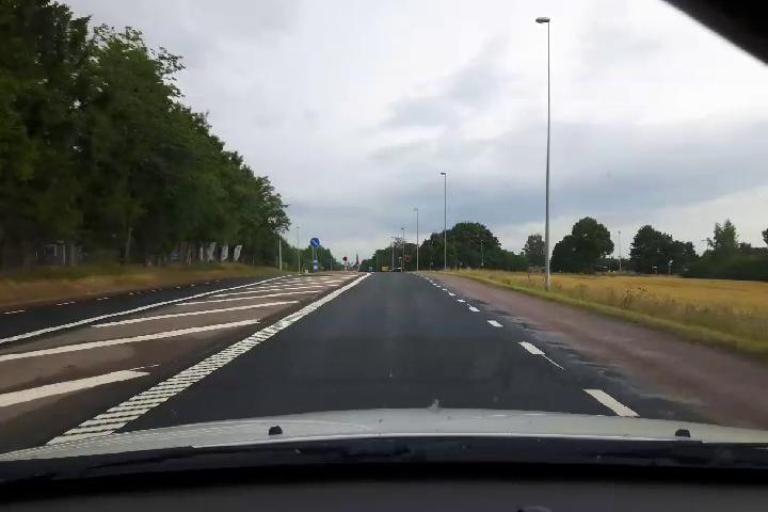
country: SE
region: Uppsala
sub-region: Uppsala Kommun
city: Gamla Uppsala
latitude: 59.8831
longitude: 17.6207
